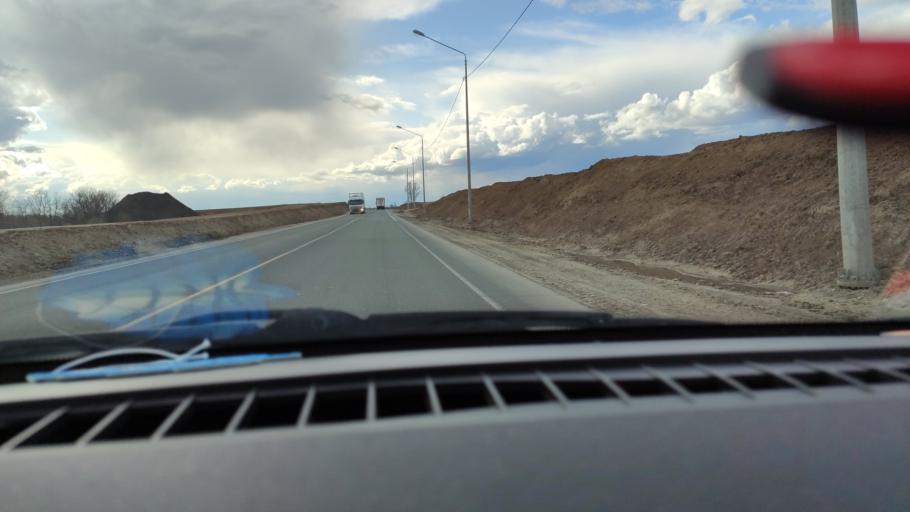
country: RU
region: Saratov
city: Sennoy
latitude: 52.1609
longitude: 47.0528
